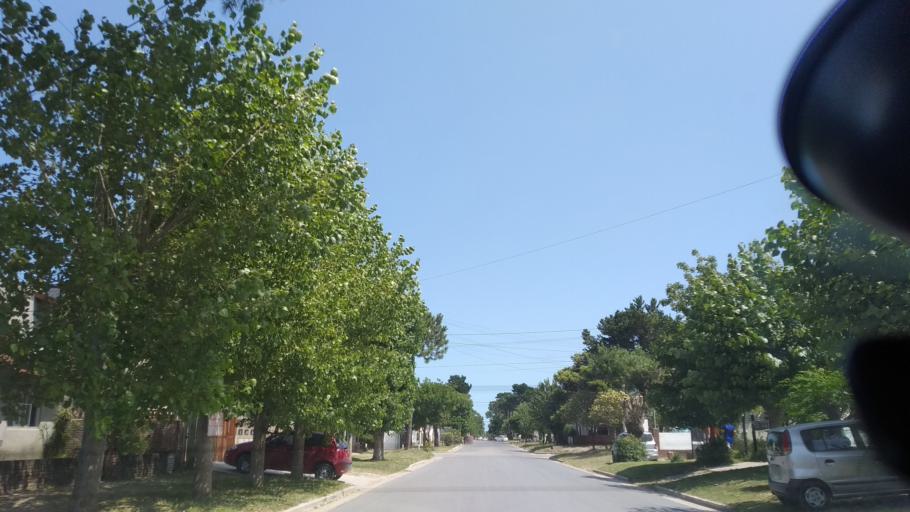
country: AR
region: Buenos Aires
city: Mar del Tuyu
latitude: -36.5747
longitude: -56.6938
